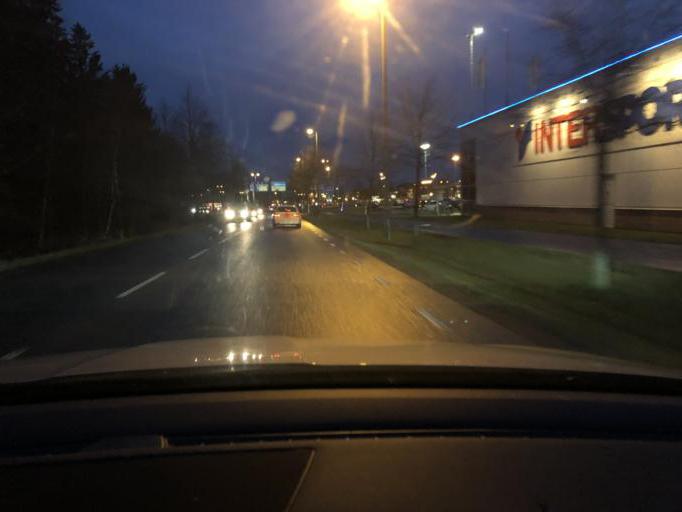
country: SE
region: Joenkoeping
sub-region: Jonkopings Kommun
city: Jonkoping
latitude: 57.7685
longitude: 14.2004
